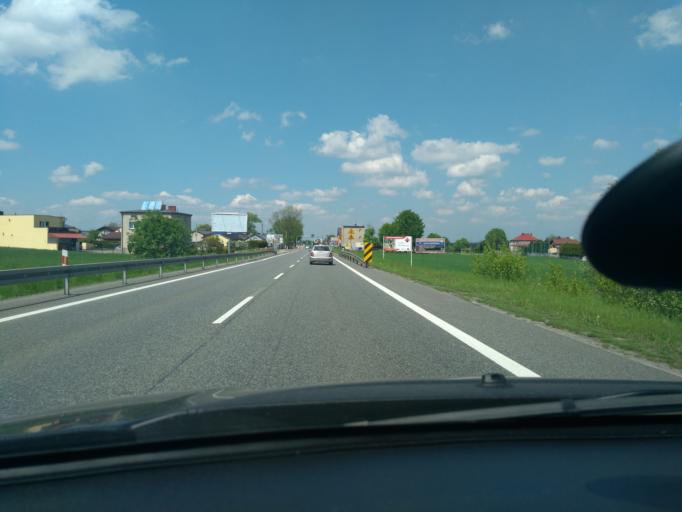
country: PL
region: Silesian Voivodeship
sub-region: Powiat mikolowski
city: Mikolow
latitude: 50.1988
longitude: 18.8637
